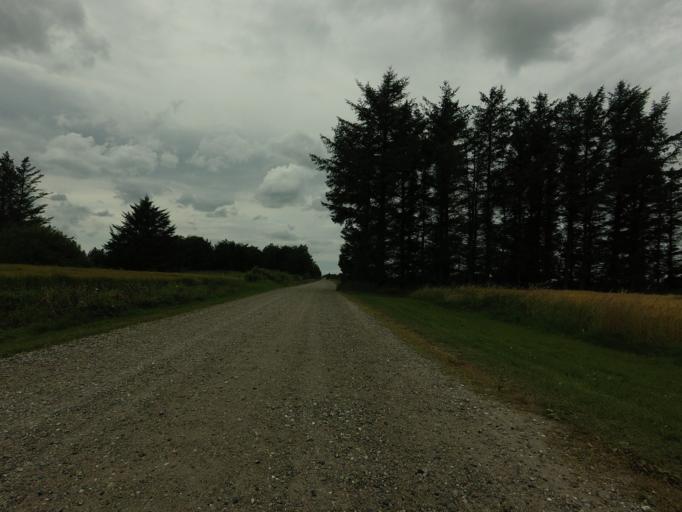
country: DK
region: North Denmark
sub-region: Jammerbugt Kommune
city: Pandrup
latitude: 57.3387
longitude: 9.7050
